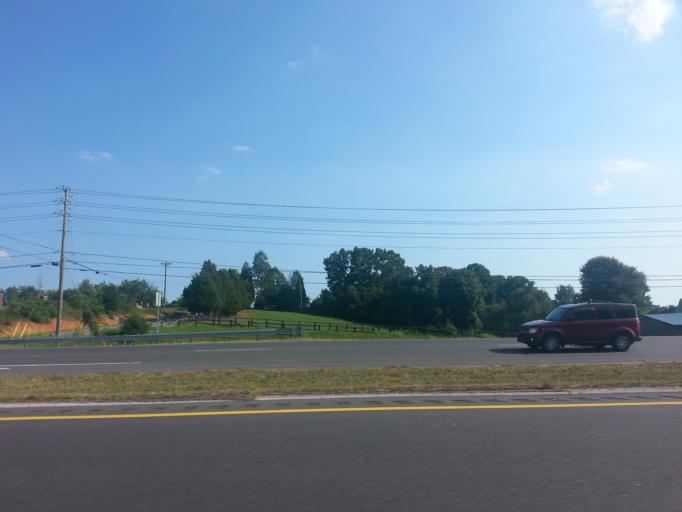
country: US
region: Tennessee
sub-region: Blount County
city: Louisville
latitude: 35.7558
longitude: -84.0759
